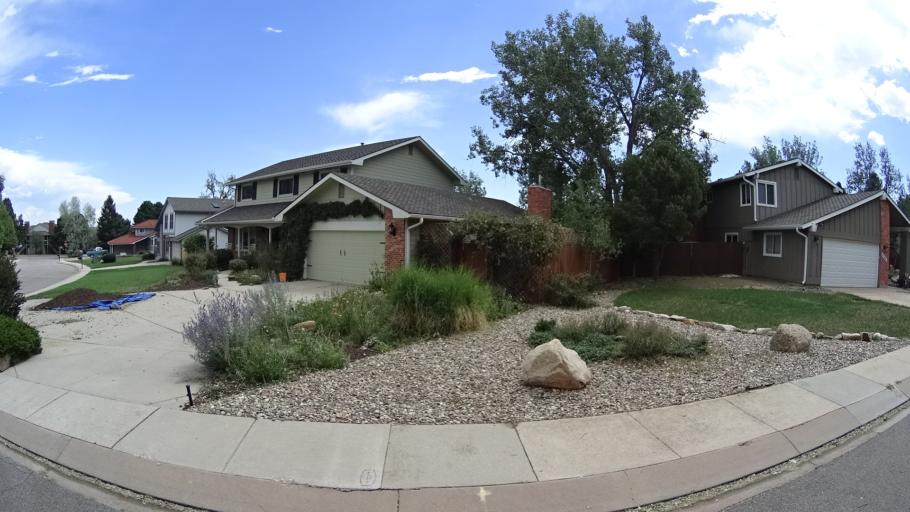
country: US
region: Colorado
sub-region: El Paso County
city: Stratmoor
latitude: 38.7722
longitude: -104.8158
